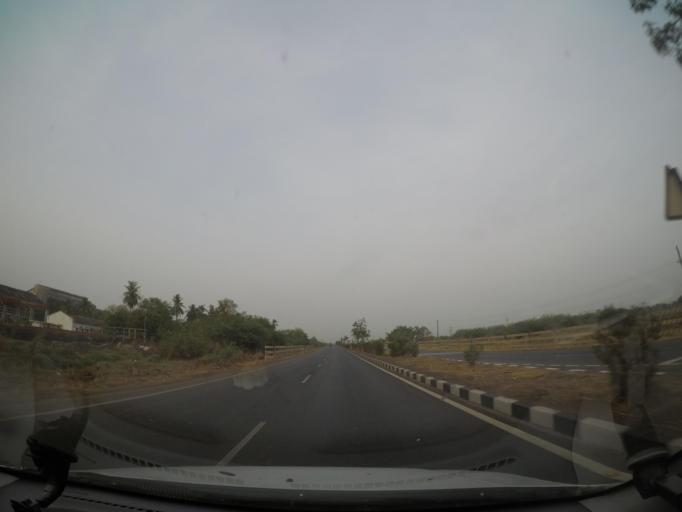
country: IN
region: Andhra Pradesh
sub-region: Krishna
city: Gannavaram
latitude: 16.6232
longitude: 80.9352
